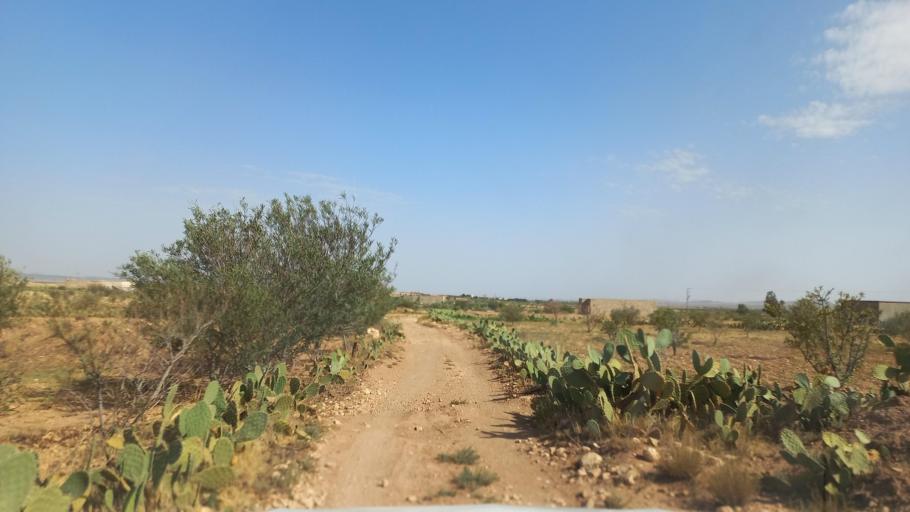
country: TN
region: Al Qasrayn
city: Kasserine
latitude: 35.2808
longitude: 8.9536
